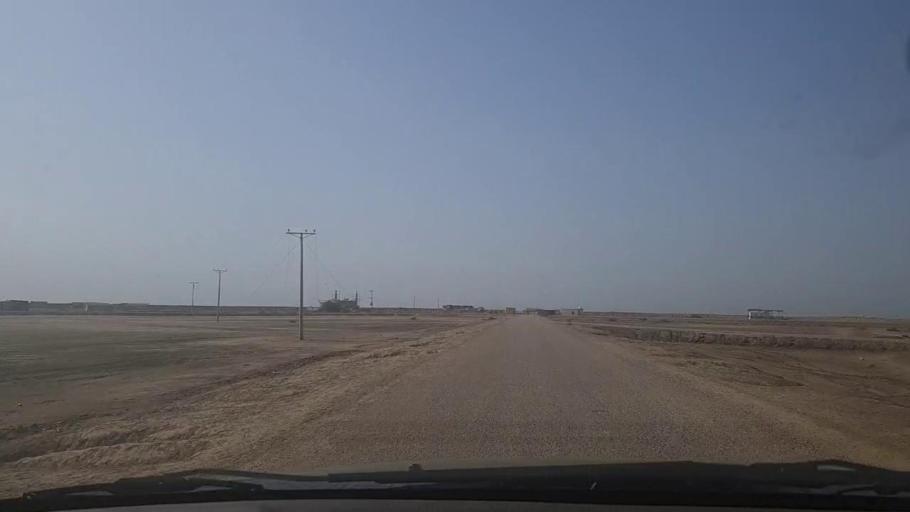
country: PK
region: Sindh
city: Keti Bandar
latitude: 24.1814
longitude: 67.5057
